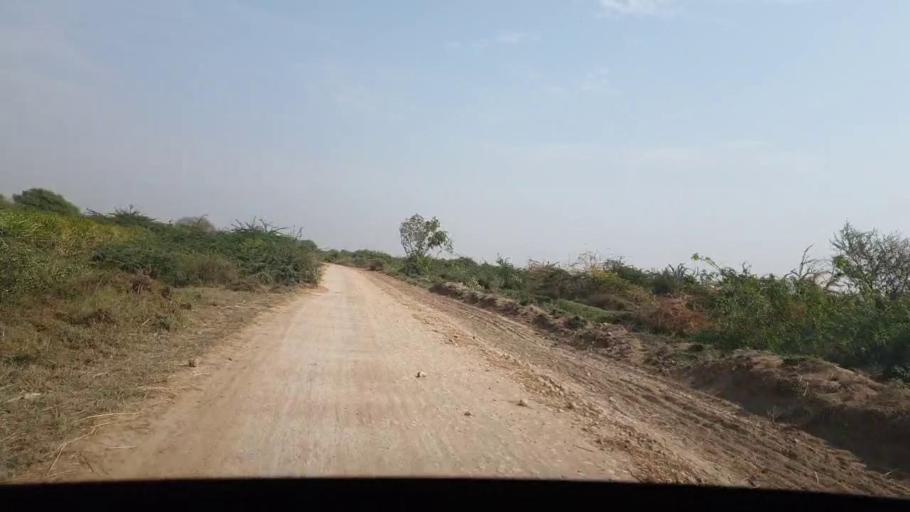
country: PK
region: Sindh
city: Chuhar Jamali
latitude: 24.2686
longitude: 67.9183
